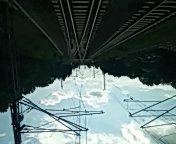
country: DE
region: Brandenburg
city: Halbe
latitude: 52.1157
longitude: 13.6940
